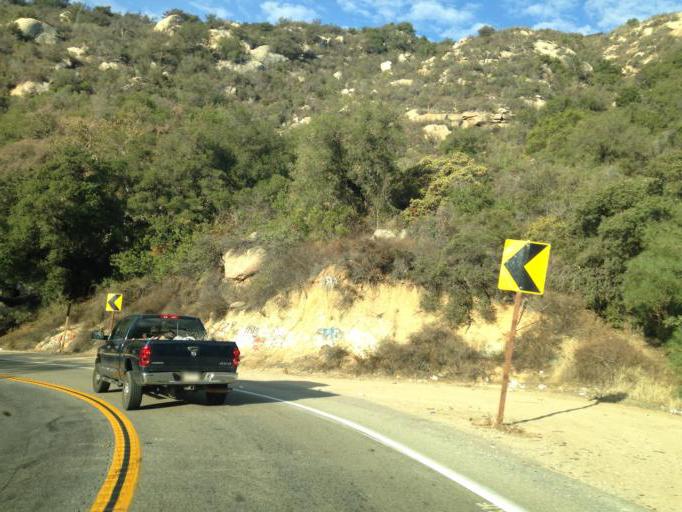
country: US
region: California
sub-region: San Diego County
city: Rainbow
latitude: 33.4089
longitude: -117.0848
